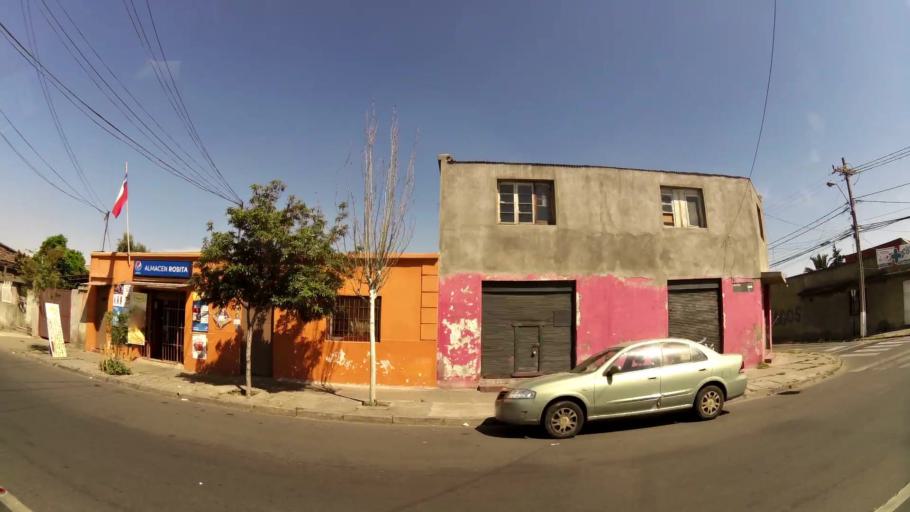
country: CL
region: Santiago Metropolitan
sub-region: Provincia de Santiago
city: Santiago
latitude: -33.5159
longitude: -70.6426
